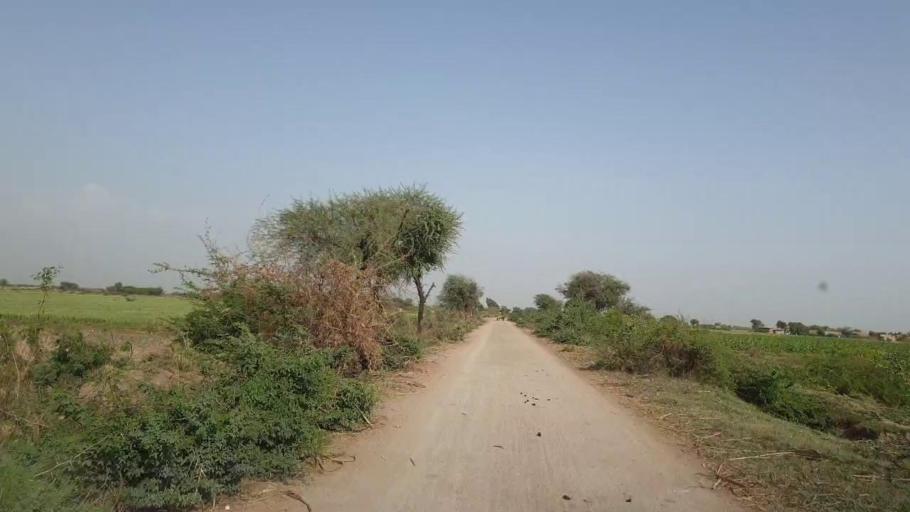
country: PK
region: Sindh
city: Tando Ghulam Ali
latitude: 25.0733
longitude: 68.8572
